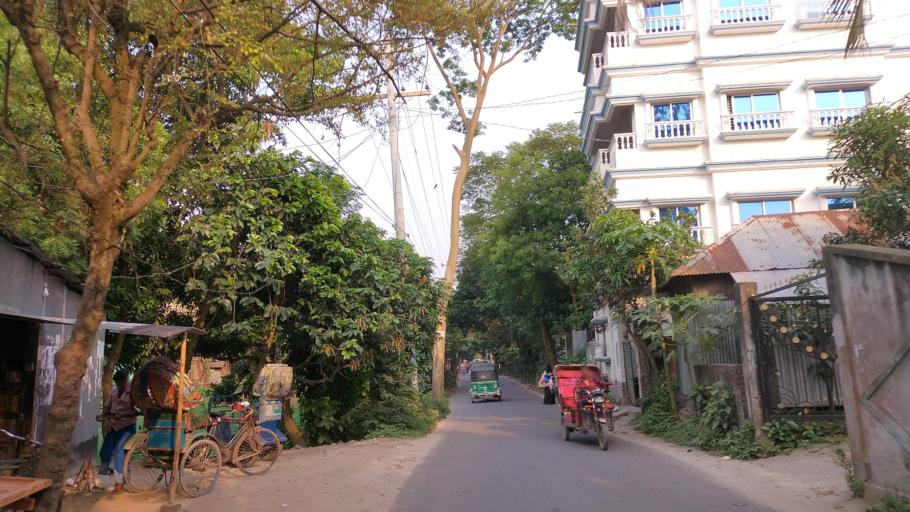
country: BD
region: Dhaka
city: Azimpur
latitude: 23.6652
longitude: 90.3296
